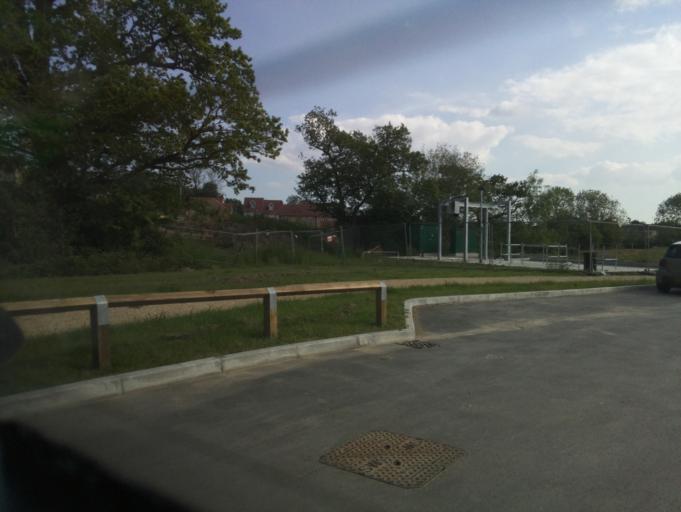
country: GB
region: England
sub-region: Wiltshire
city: Chippenham
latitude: 51.4733
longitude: -2.1158
